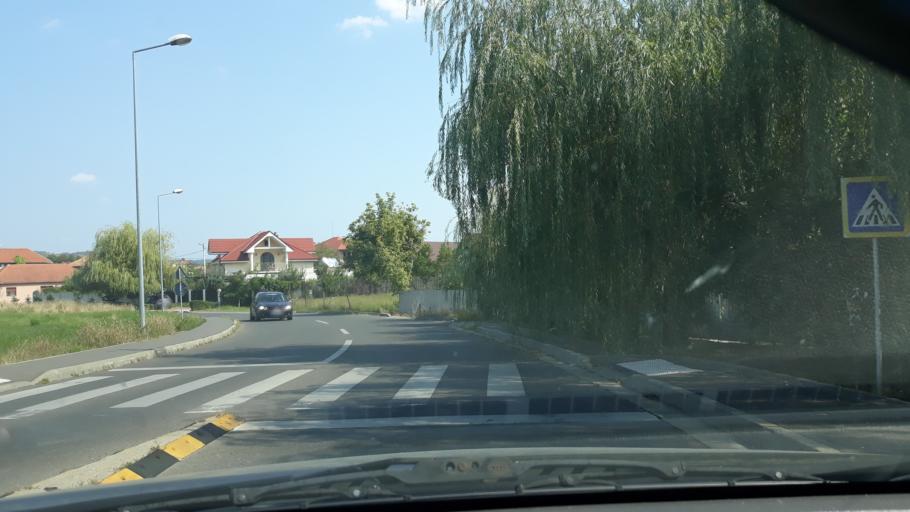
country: RO
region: Bihor
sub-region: Comuna Biharea
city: Oradea
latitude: 47.0376
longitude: 21.9516
